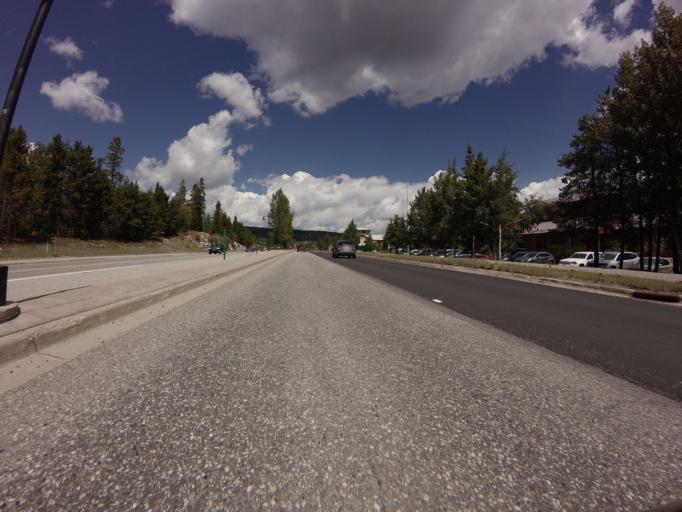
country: US
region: Colorado
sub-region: Summit County
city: Frisco
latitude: 39.5832
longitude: -106.0938
